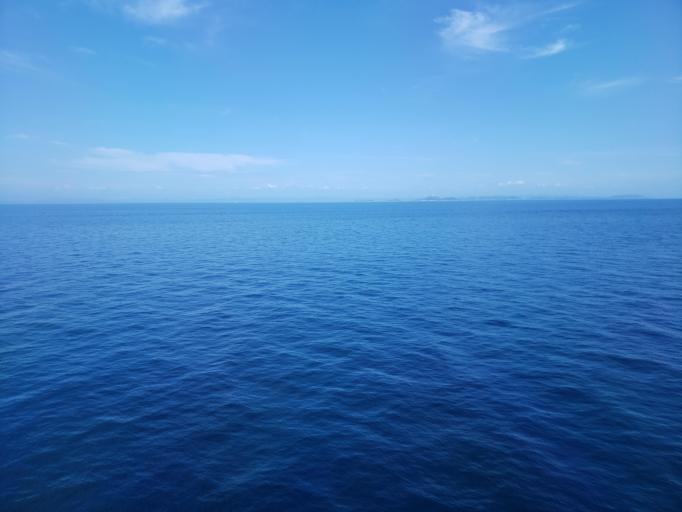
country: JP
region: Tokushima
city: Narutocho-mitsuishi
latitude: 34.4737
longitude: 134.5069
